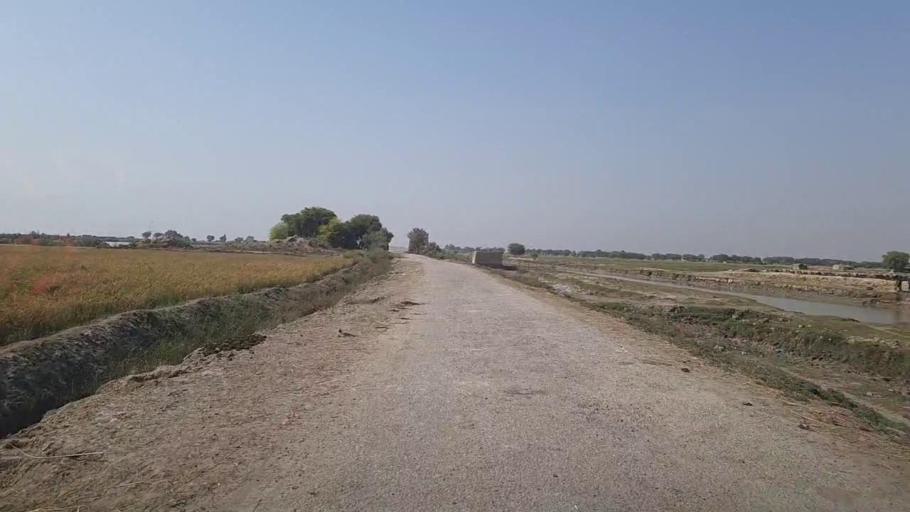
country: PK
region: Sindh
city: Kandhkot
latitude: 28.4156
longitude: 69.2350
